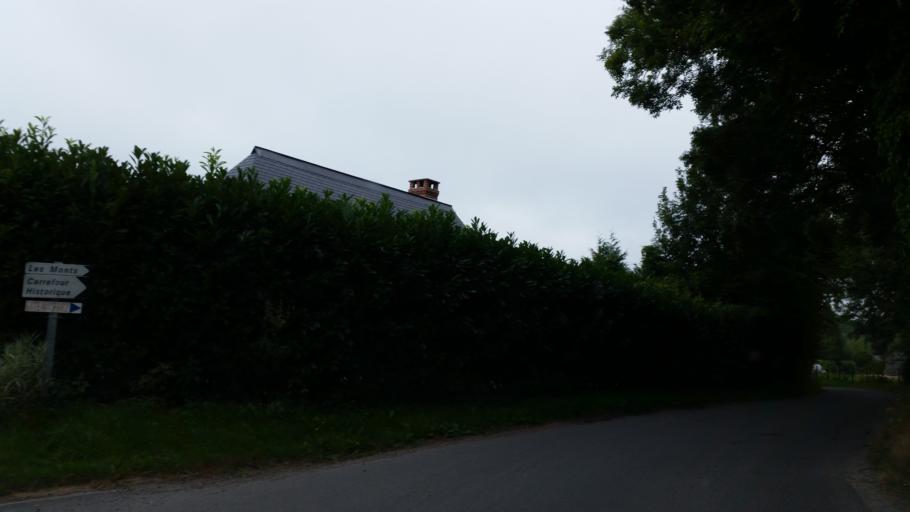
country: FR
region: Lower Normandy
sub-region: Departement du Calvados
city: Equemauville
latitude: 49.3891
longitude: 0.2371
